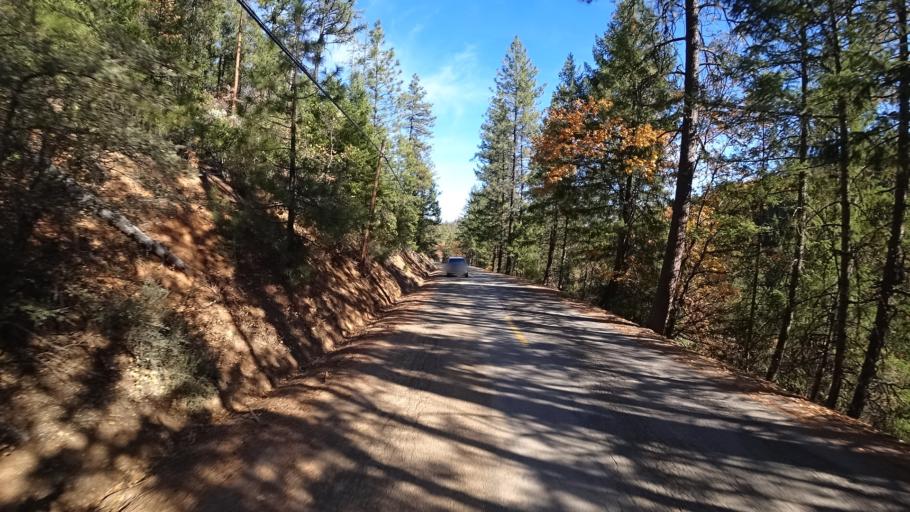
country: US
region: California
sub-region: Siskiyou County
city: Yreka
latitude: 41.7285
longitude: -122.7129
